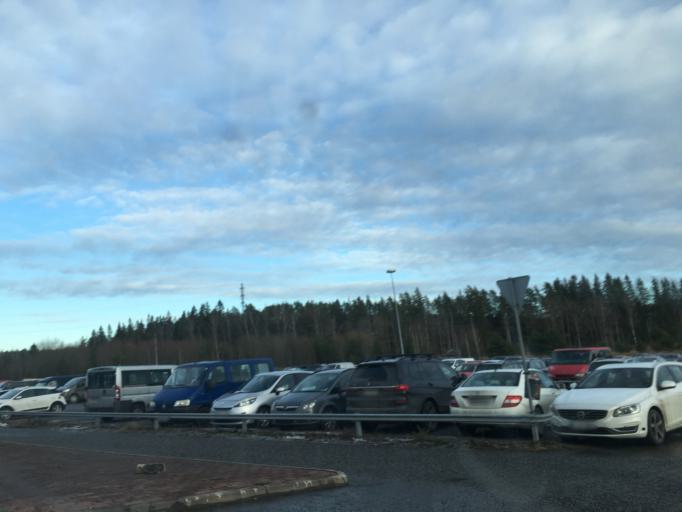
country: FI
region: Varsinais-Suomi
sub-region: Turku
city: Raisio
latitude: 60.4617
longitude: 22.1340
